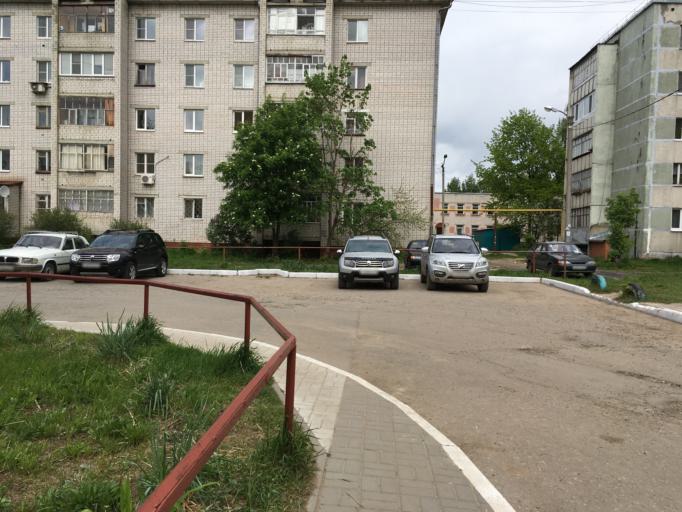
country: RU
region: Mariy-El
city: Yoshkar-Ola
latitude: 56.6485
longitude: 47.8606
